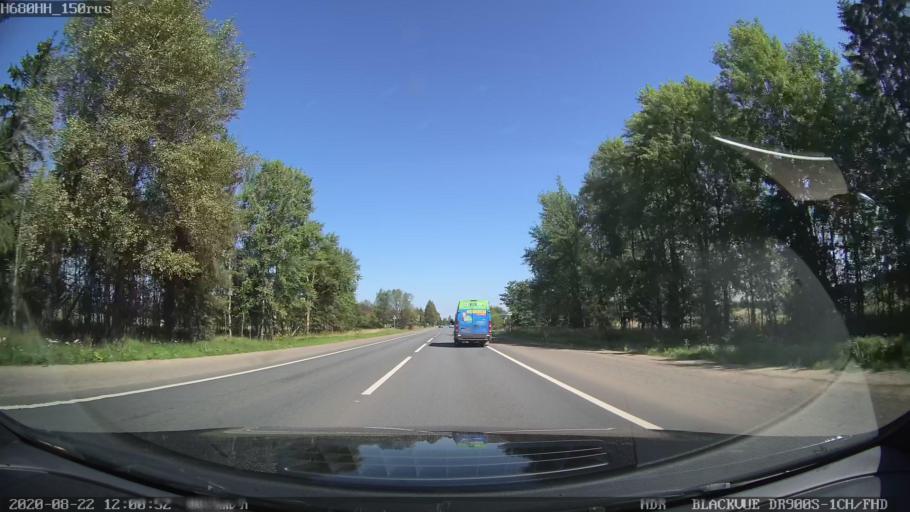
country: RU
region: Tverskaya
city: Rameshki
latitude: 57.2236
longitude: 36.0952
